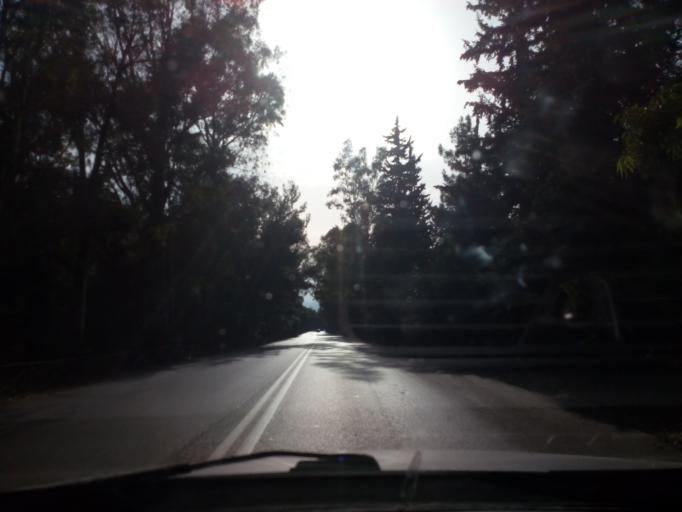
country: GR
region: Attica
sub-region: Nomos Attikis
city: Zografos
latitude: 37.9657
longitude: 23.7872
